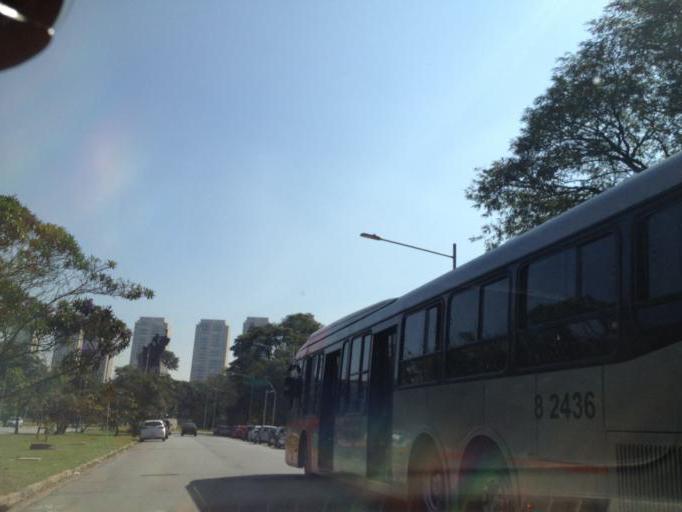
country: BR
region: Sao Paulo
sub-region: Osasco
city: Osasco
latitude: -23.5577
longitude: -46.7327
